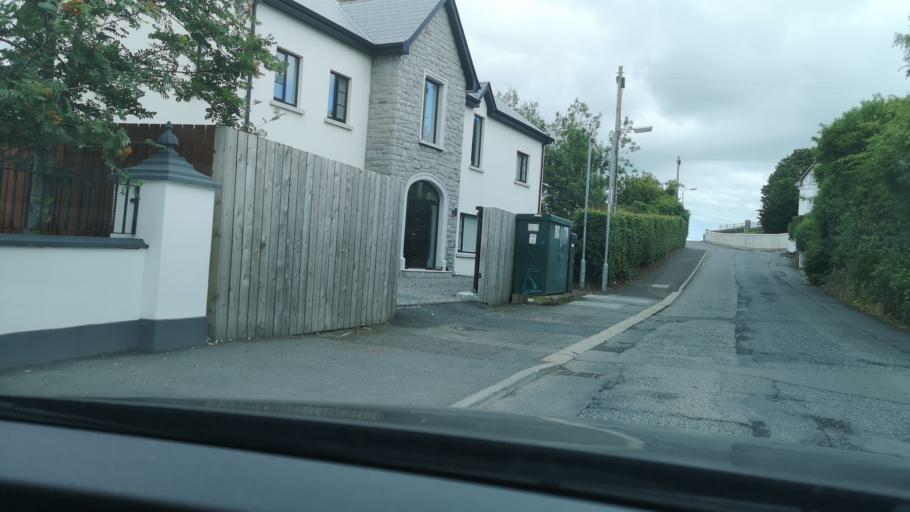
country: GB
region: Northern Ireland
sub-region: Newry and Mourne District
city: Newry
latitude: 54.1716
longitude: -6.3284
